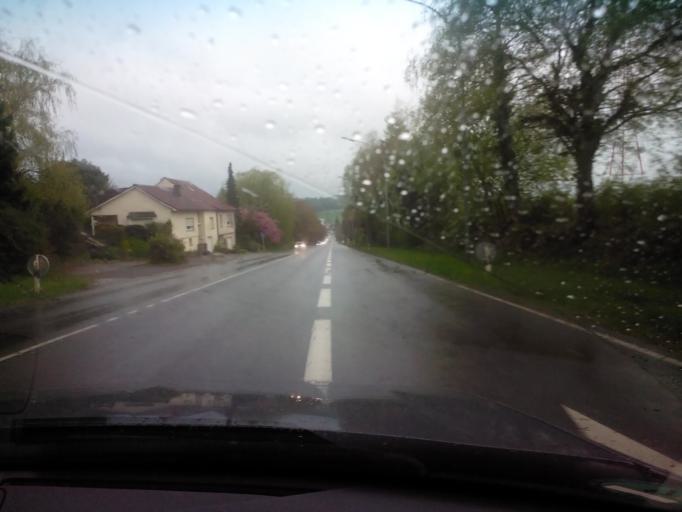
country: LU
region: Grevenmacher
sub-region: Canton de Grevenmacher
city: Junglinster
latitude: 49.7170
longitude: 6.2655
